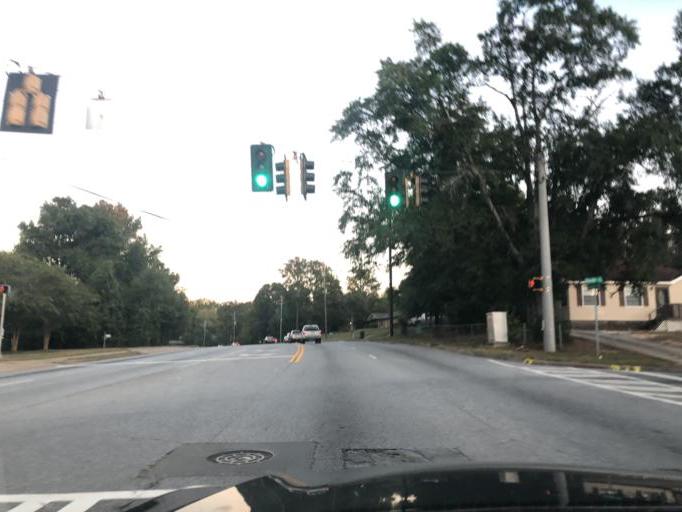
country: US
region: Georgia
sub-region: Muscogee County
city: Columbus
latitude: 32.4658
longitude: -84.9014
